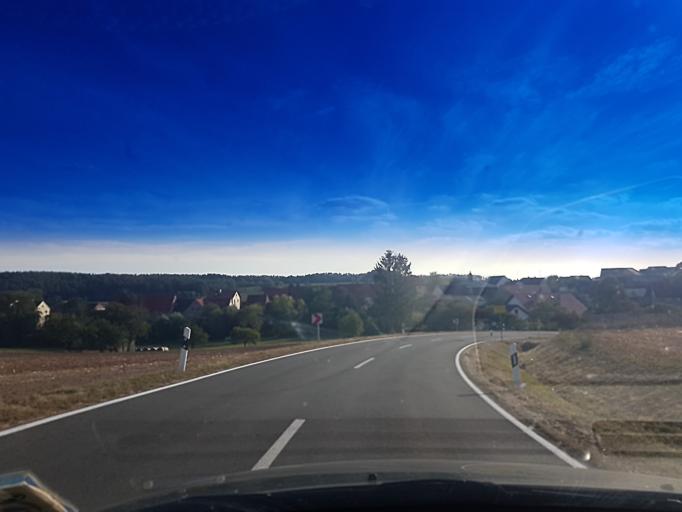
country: DE
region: Bavaria
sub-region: Upper Franconia
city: Schlusselfeld
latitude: 49.7685
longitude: 10.6602
